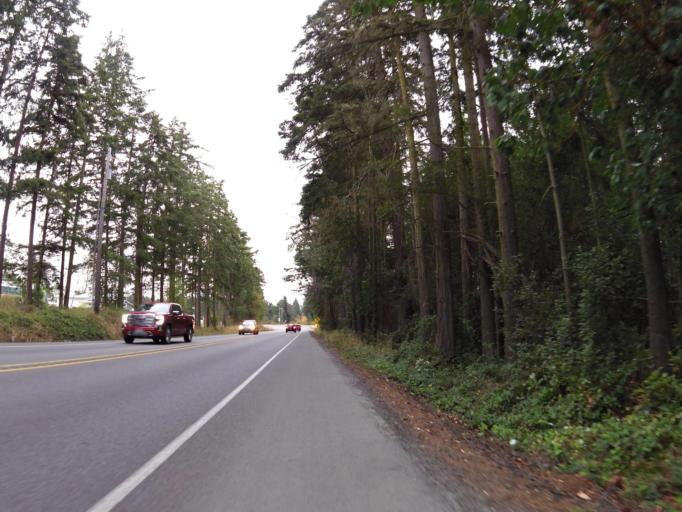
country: US
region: Washington
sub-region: Jefferson County
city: Port Hadlock-Irondale
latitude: 48.0745
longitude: -122.8186
